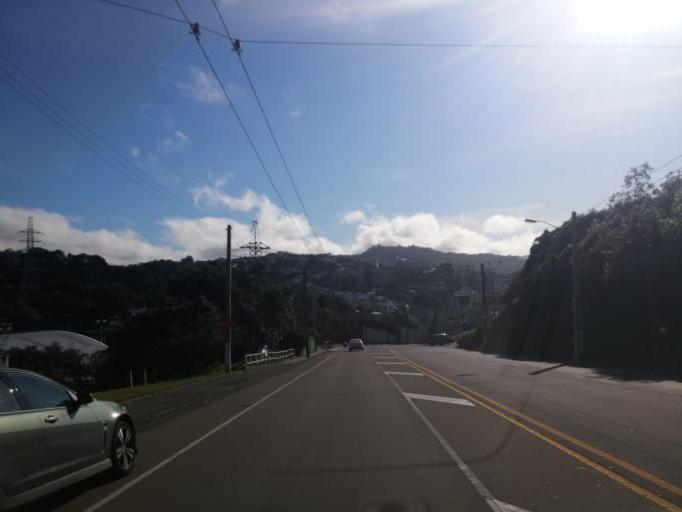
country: NZ
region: Wellington
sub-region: Wellington City
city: Wellington
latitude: -41.3019
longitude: 174.7696
